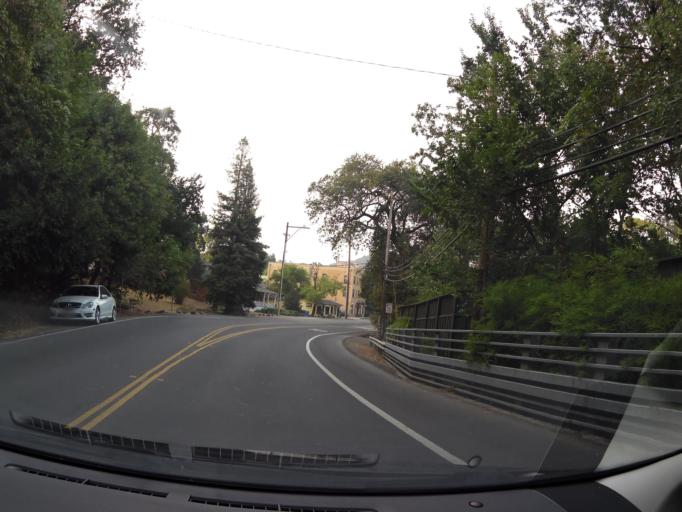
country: US
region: California
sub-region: Sonoma County
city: Eldridge
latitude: 38.3611
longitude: -122.5257
